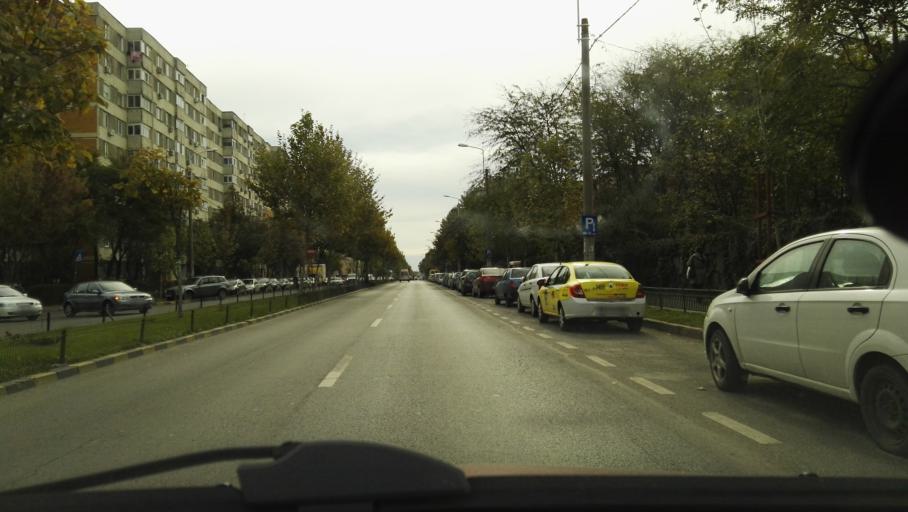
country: RO
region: Ilfov
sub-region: Comuna Popesti-Leordeni
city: Popesti-Leordeni
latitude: 44.3842
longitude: 26.1304
